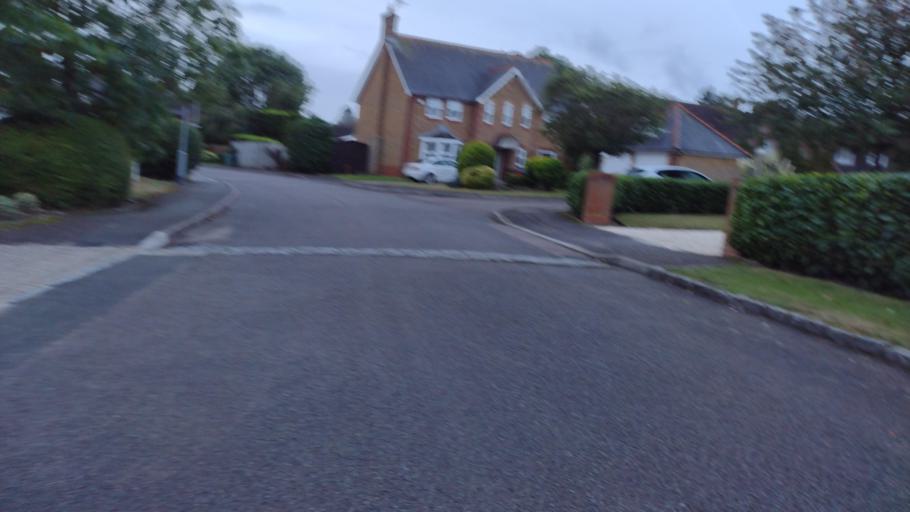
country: GB
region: England
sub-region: Wokingham
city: Winnersh
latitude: 51.4364
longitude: -0.8761
